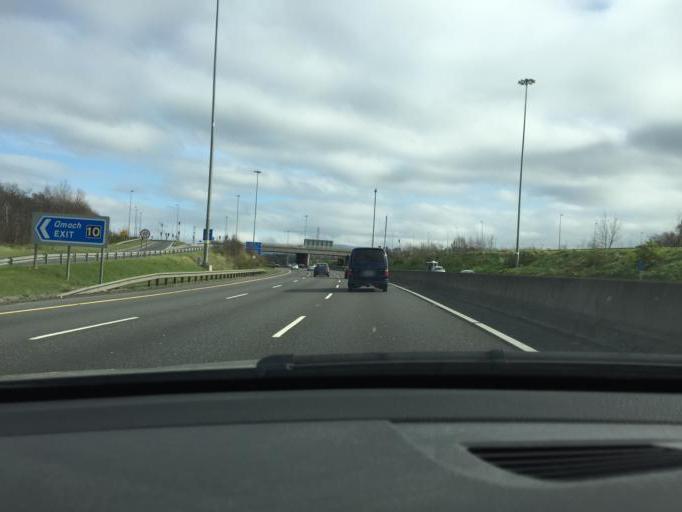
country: IE
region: Leinster
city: Tallaght
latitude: 53.3089
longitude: -6.3593
